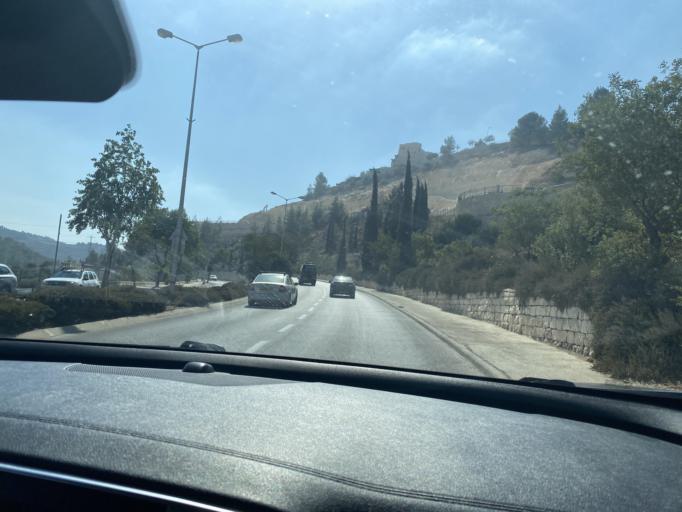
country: PS
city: Khallat Hamamah
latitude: 31.7487
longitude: 35.1842
